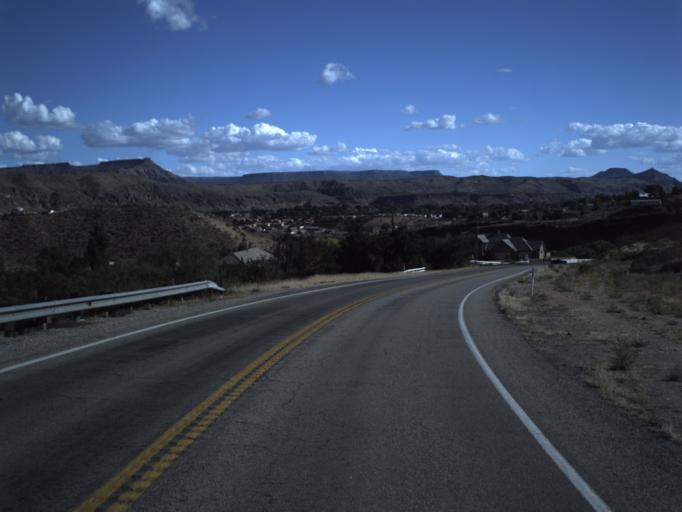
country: US
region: Utah
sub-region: Washington County
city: Toquerville
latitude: 37.2298
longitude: -113.2808
